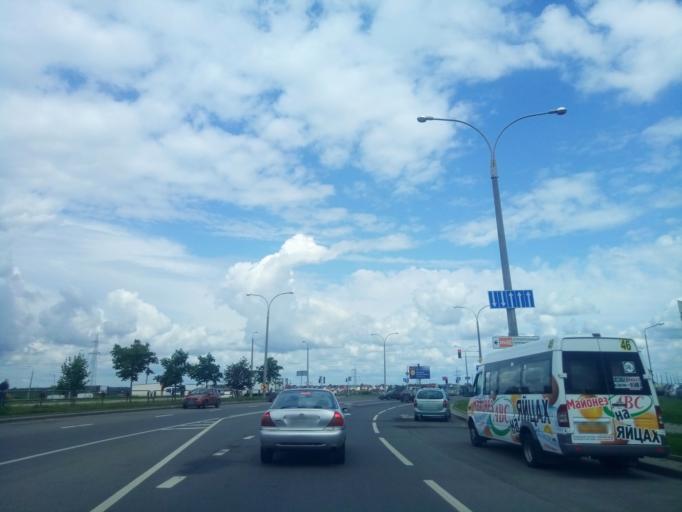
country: BY
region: Minsk
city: Zhdanovichy
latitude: 53.9129
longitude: 27.4149
